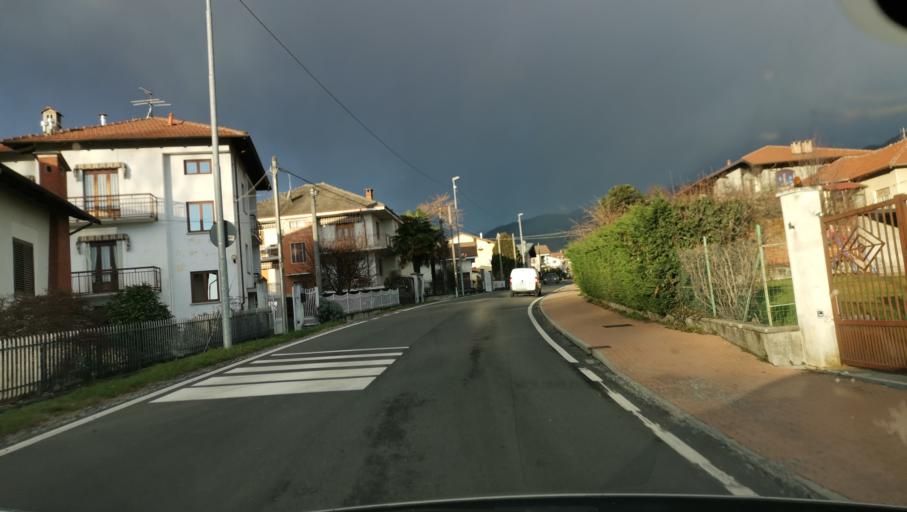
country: IT
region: Piedmont
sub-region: Provincia di Torino
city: Giaveno
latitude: 45.0459
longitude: 7.3467
